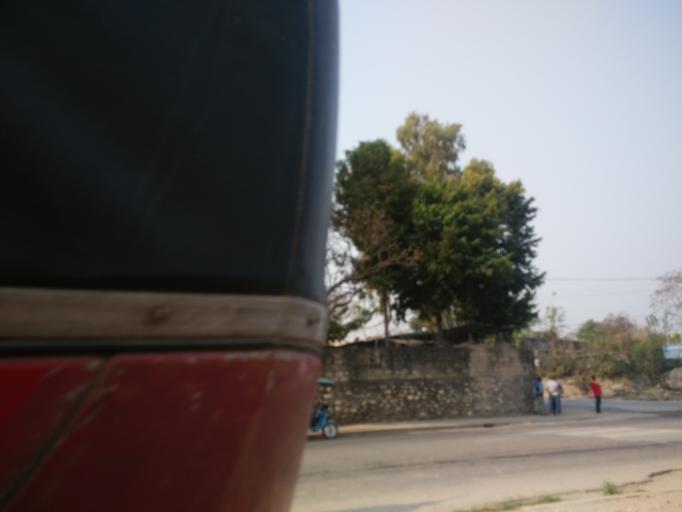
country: NP
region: Central Region
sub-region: Narayani Zone
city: Hitura
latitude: 27.4321
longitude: 85.0281
